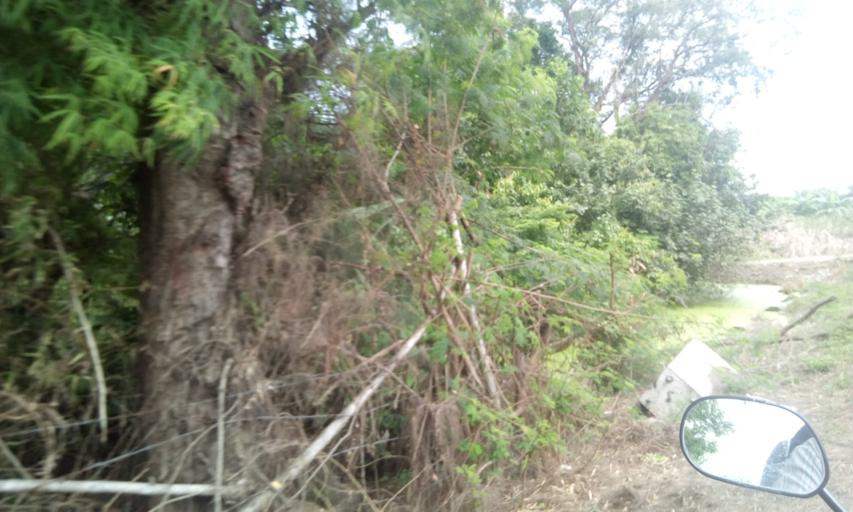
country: TH
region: Pathum Thani
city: Ban Lam Luk Ka
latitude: 14.0048
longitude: 100.8422
